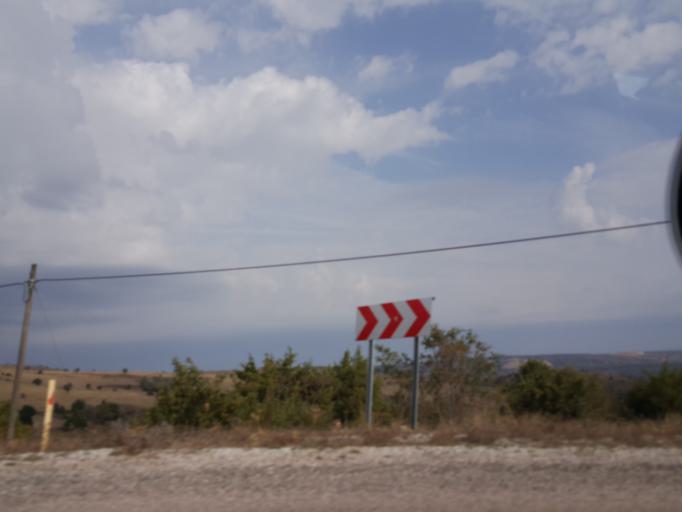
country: TR
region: Tokat
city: Zile
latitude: 40.3982
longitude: 35.8594
